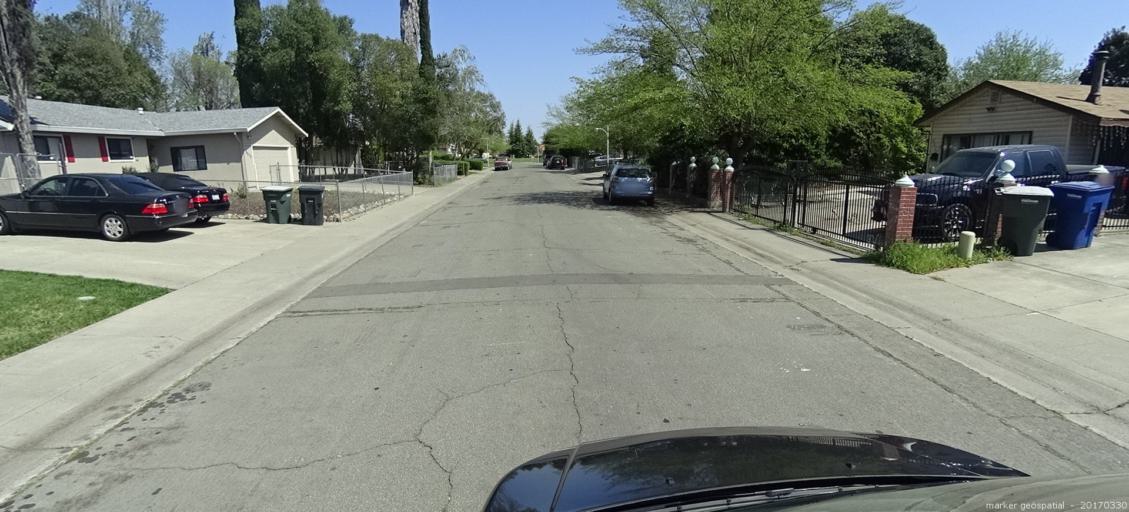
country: US
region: California
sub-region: Sacramento County
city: Florin
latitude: 38.4644
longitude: -121.4229
